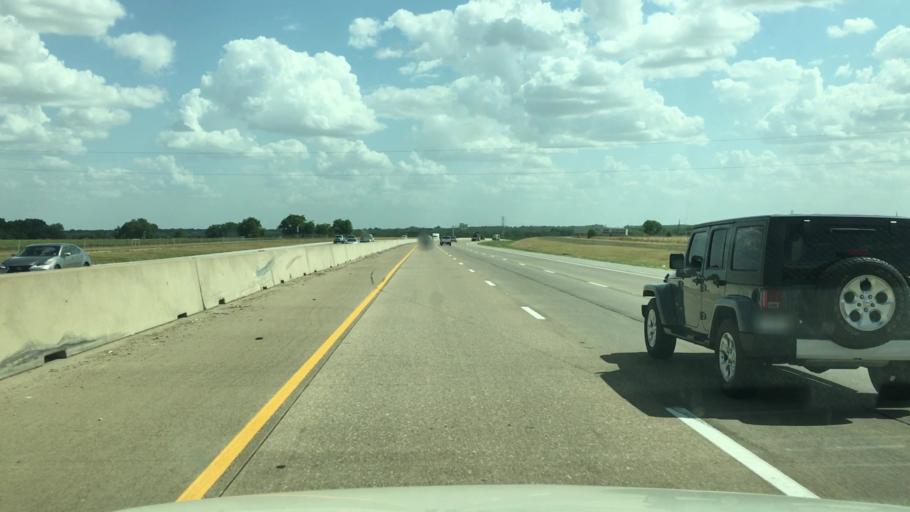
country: US
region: Texas
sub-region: Ellis County
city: Italy
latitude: 32.2460
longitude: -96.8758
